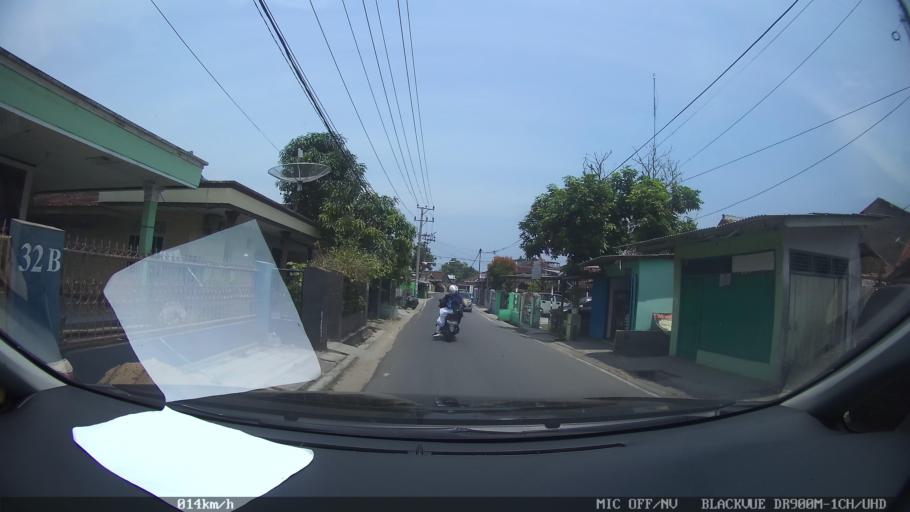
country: ID
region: Lampung
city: Bandarlampung
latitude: -5.4480
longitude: 105.2547
